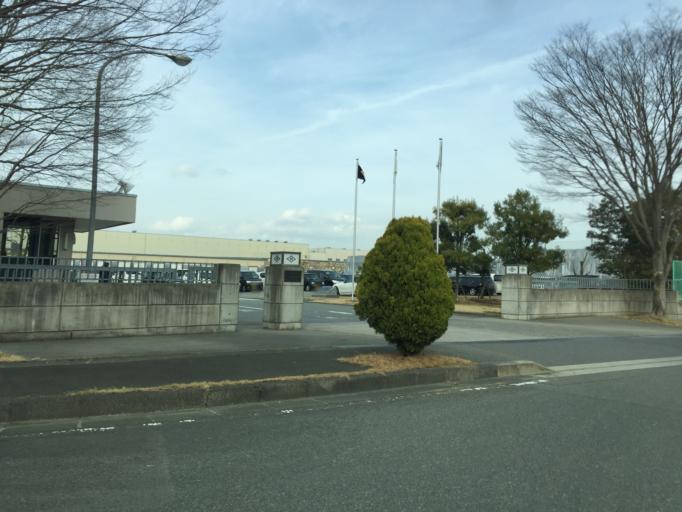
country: JP
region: Ibaraki
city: Kitaibaraki
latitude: 36.9353
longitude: 140.7421
